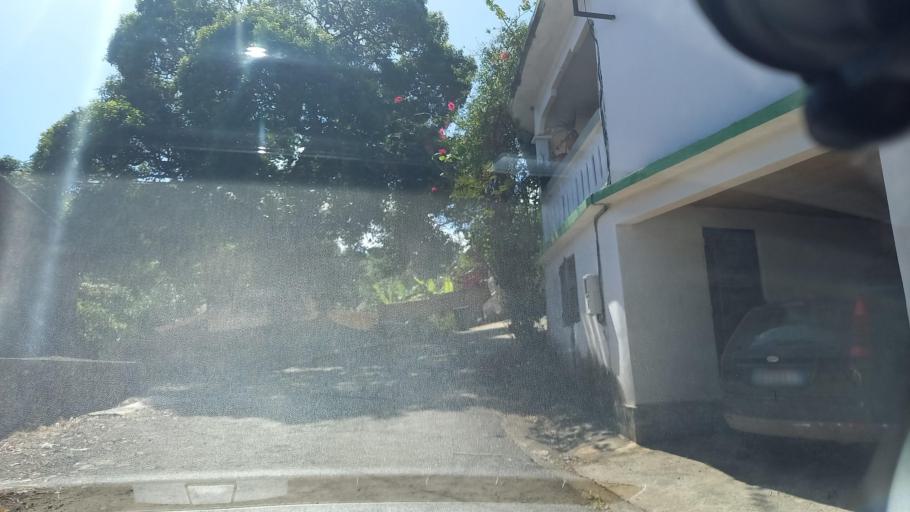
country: YT
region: Kani-Keli
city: Kani Keli
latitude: -12.9646
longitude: 45.1128
